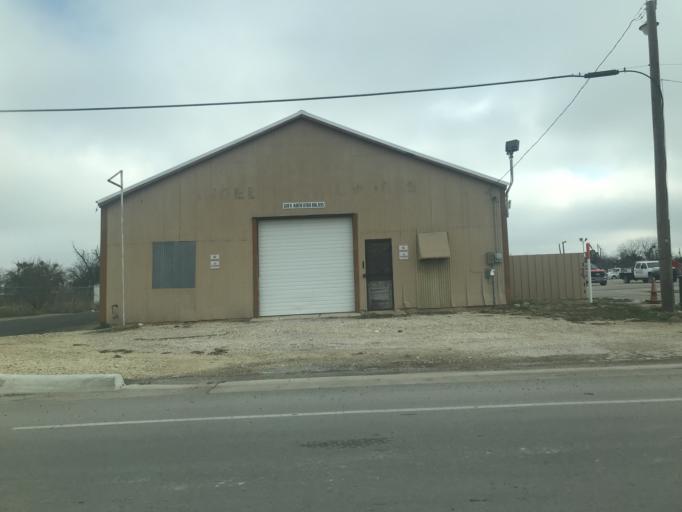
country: US
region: Texas
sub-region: Tom Green County
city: San Angelo
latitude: 31.4850
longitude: -100.4565
